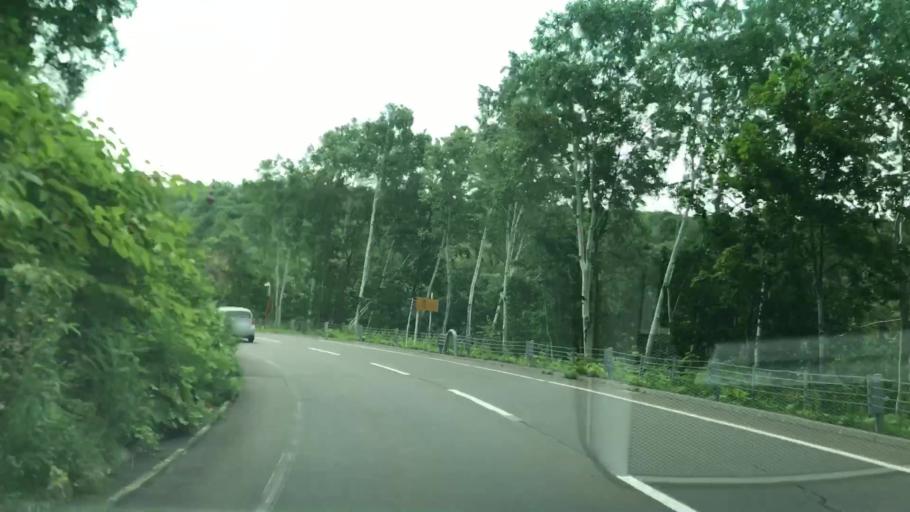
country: JP
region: Hokkaido
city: Yoichi
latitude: 43.1297
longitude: 140.8262
